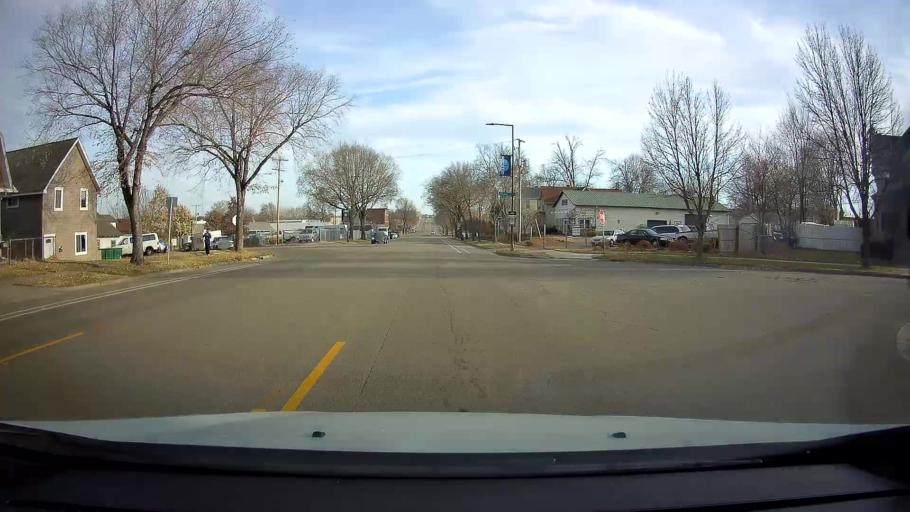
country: US
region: Minnesota
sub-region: Ramsey County
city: Saint Paul
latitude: 44.9685
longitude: -93.1234
